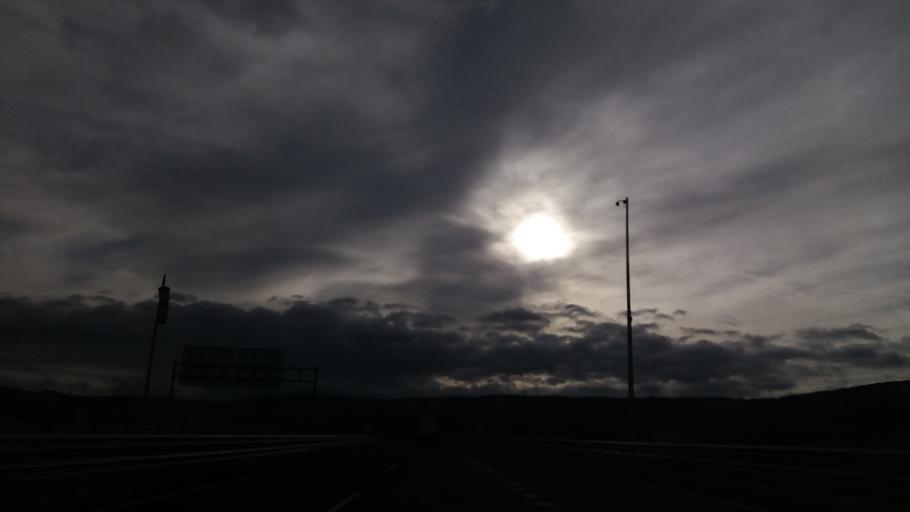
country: ES
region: Basque Country
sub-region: Provincia de Alava
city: Salvatierra
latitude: 42.8462
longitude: -2.4187
